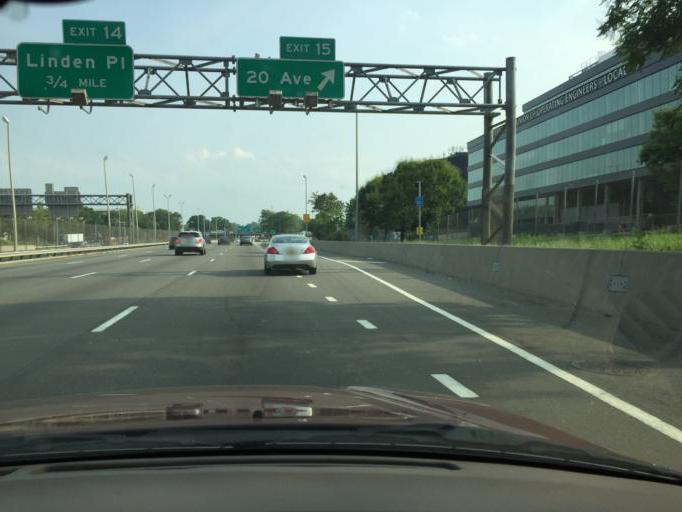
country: US
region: New York
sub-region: Bronx
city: The Bronx
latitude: 40.7852
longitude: -73.8246
